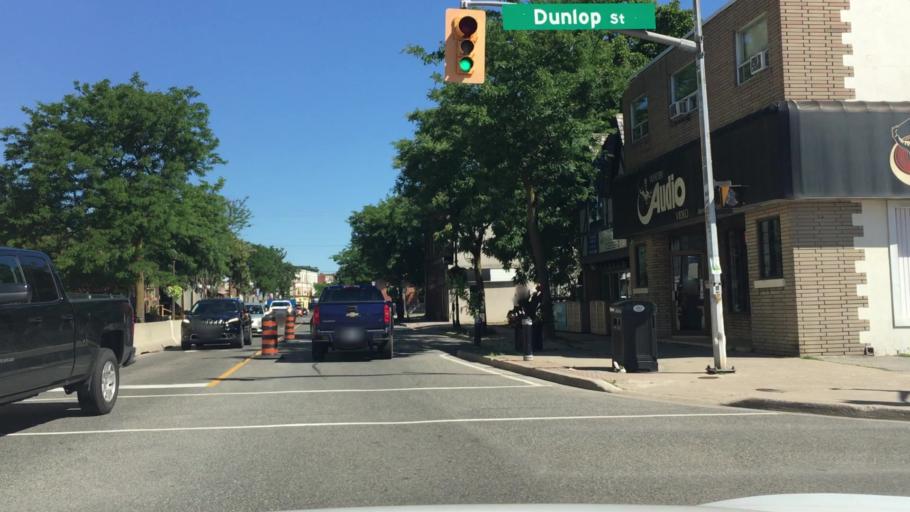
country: CA
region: Ontario
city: Oshawa
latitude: 43.8778
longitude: -78.9413
